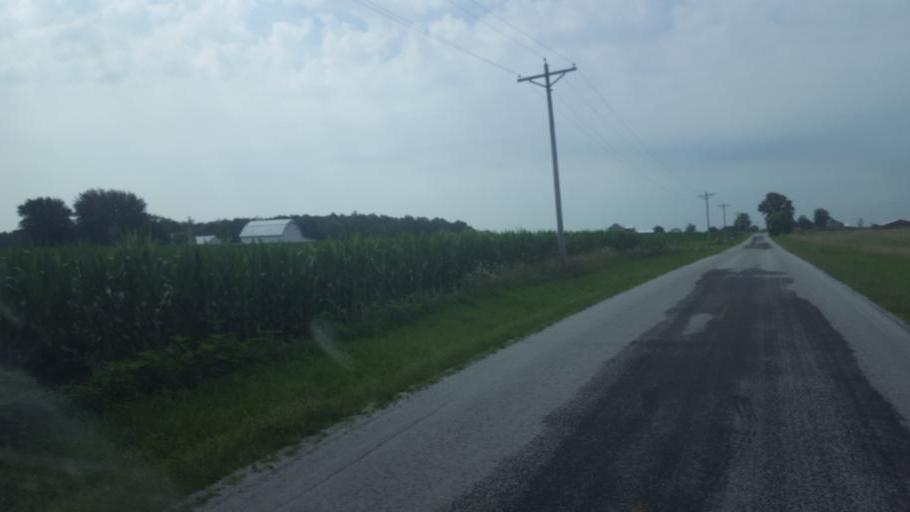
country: US
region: Ohio
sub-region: Hardin County
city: Kenton
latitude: 40.6392
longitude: -83.5380
